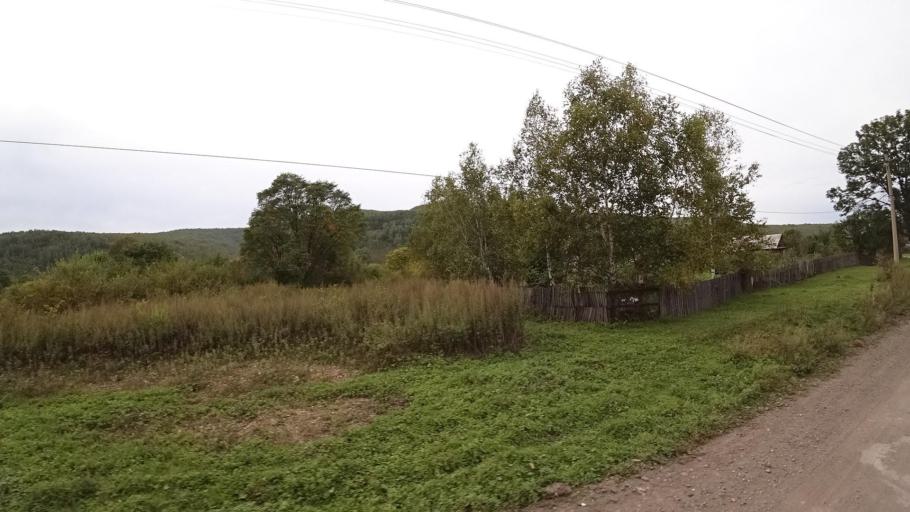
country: RU
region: Jewish Autonomous Oblast
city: Khingansk
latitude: 49.0371
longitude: 131.0495
